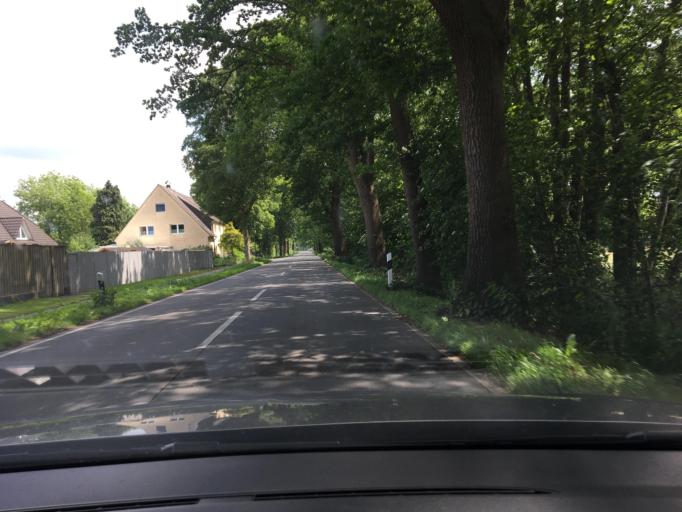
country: DE
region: Lower Saxony
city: Osterholz-Scharmbeck
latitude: 53.2505
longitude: 8.8233
